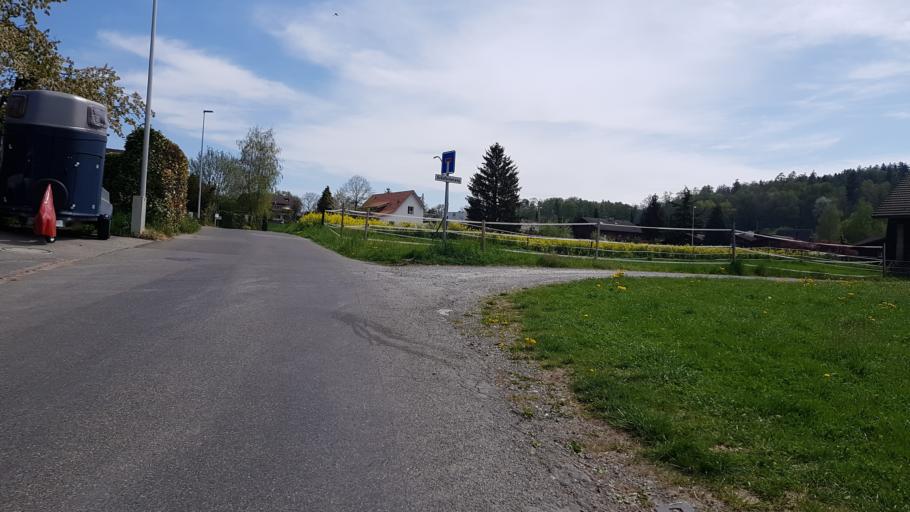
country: CH
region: Aargau
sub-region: Bezirk Kulm
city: Reinach
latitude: 47.2633
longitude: 8.1911
